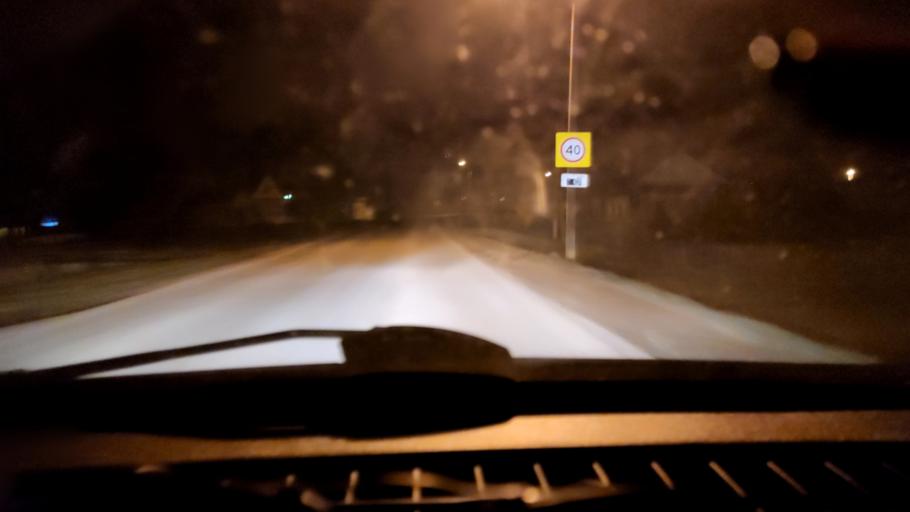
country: RU
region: Bashkortostan
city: Tolbazy
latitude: 54.0284
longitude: 55.8841
